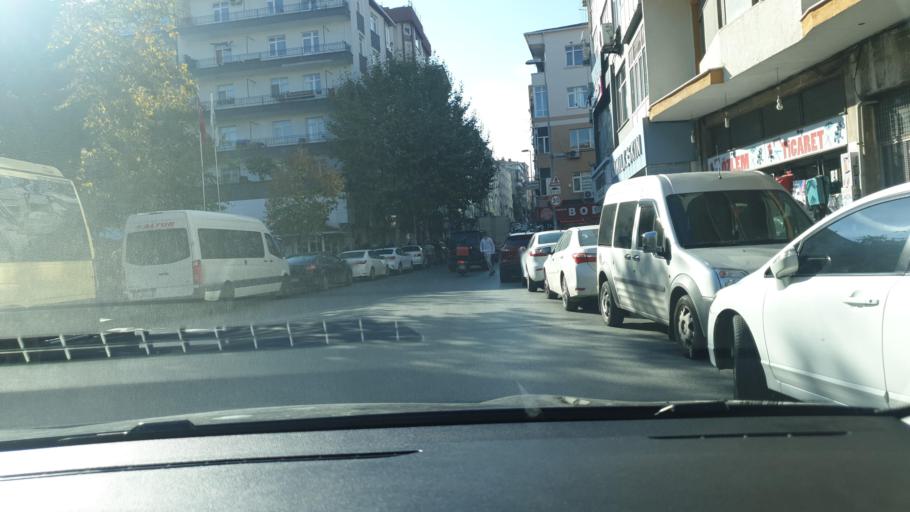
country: TR
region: Istanbul
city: Bahcelievler
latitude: 40.9947
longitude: 28.8464
